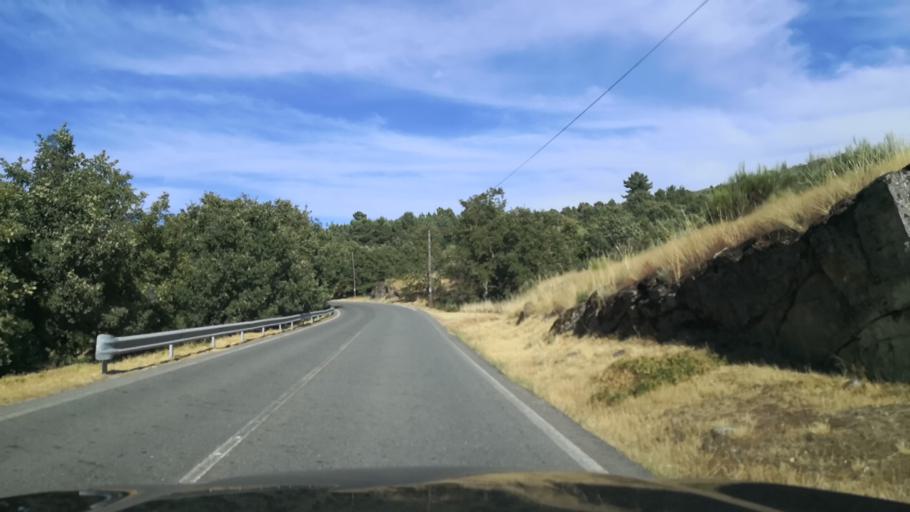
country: PT
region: Vila Real
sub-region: Murca
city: Murca
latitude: 41.3761
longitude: -7.5558
